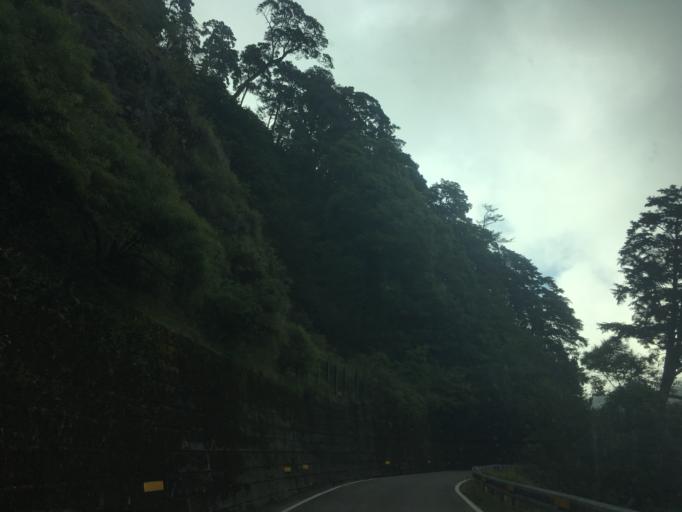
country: TW
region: Taiwan
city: Fengyuan
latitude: 24.2416
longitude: 120.9785
